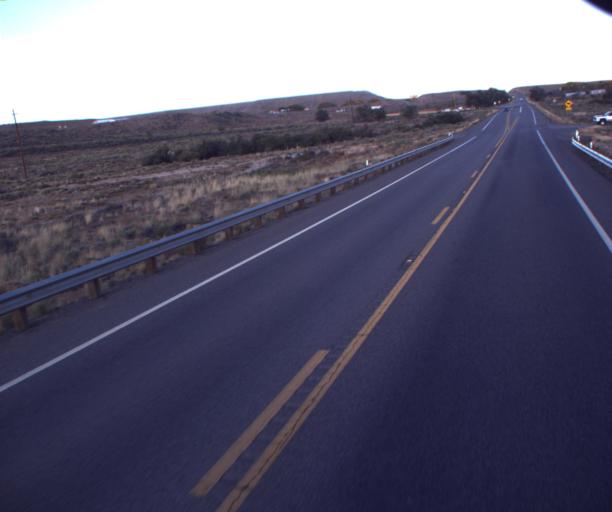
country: US
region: New Mexico
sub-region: San Juan County
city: Shiprock
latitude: 36.9285
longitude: -109.1009
